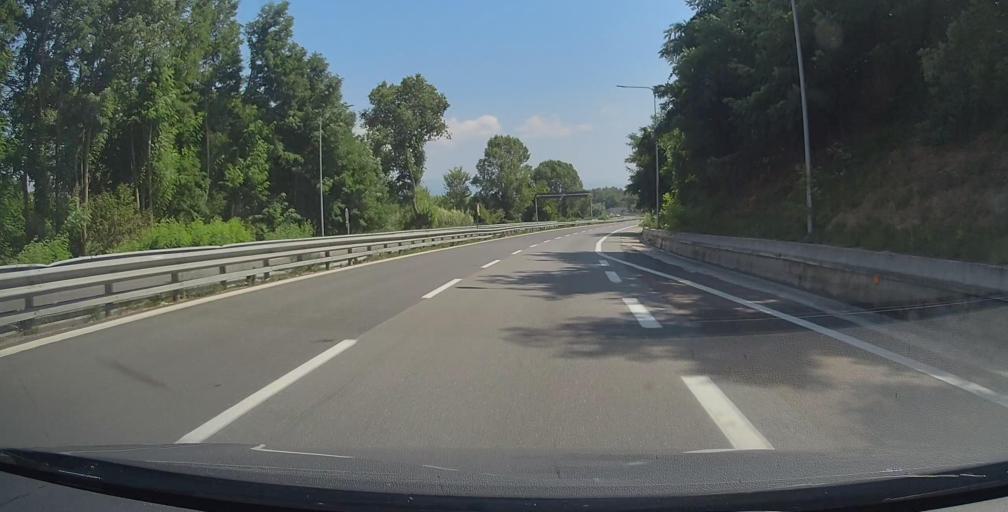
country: IT
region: Calabria
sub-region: Provincia di Vibo-Valentia
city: Sant'Onofrio
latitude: 38.7004
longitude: 16.1551
